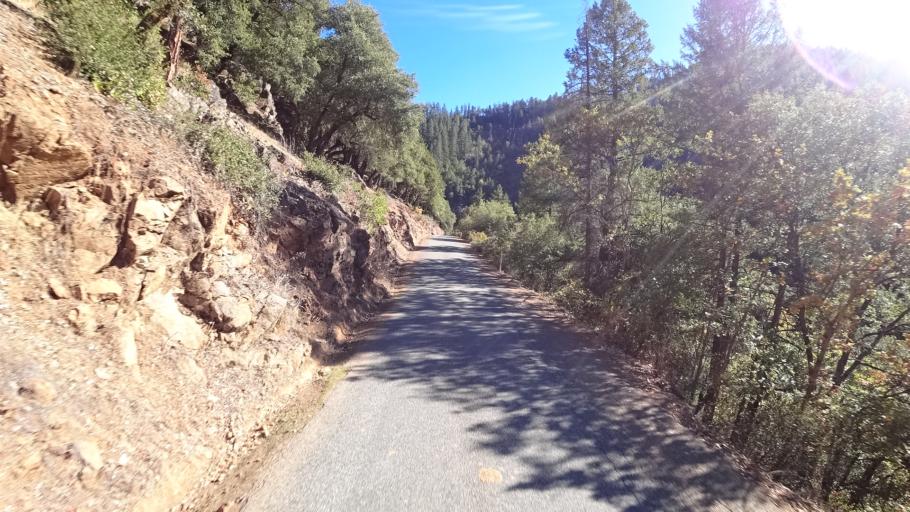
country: US
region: California
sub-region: Siskiyou County
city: Happy Camp
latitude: 41.2964
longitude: -123.1000
